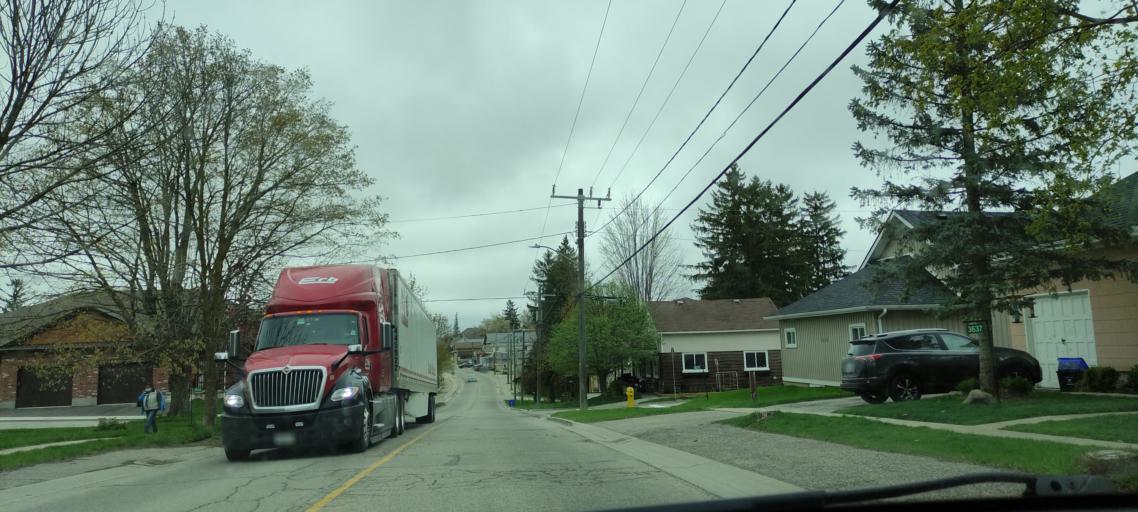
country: CA
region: Ontario
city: Stratford
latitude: 43.4734
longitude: -80.7647
